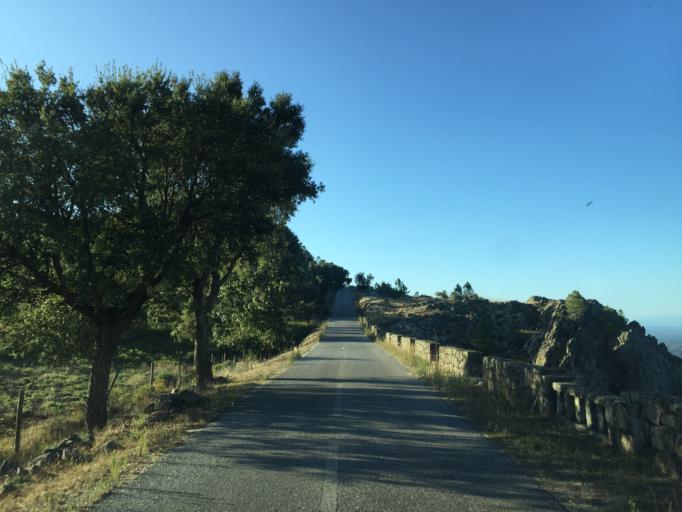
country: PT
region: Portalegre
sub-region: Castelo de Vide
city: Castelo de Vide
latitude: 39.4009
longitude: -7.4519
